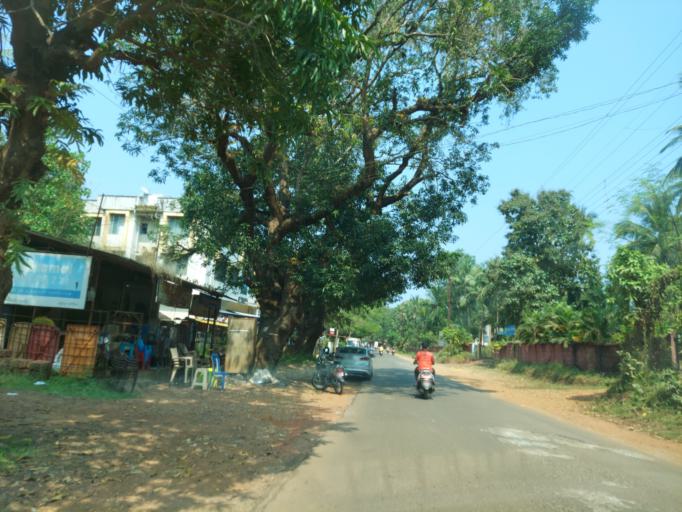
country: IN
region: Maharashtra
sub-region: Sindhudurg
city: Kudal
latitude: 16.0025
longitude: 73.6868
